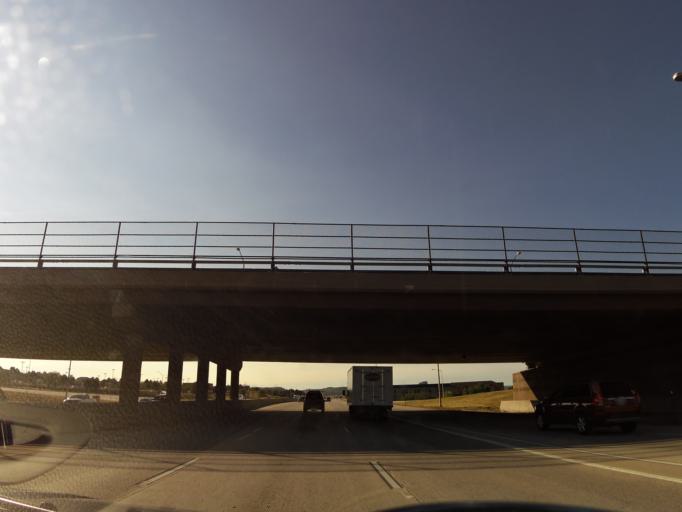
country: US
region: Colorado
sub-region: Douglas County
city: Castle Rock
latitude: 39.4131
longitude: -104.8684
